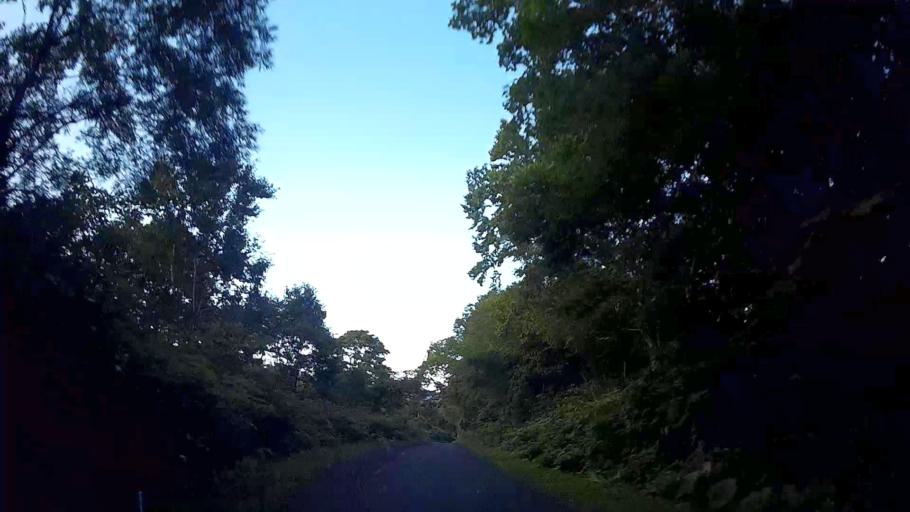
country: JP
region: Hokkaido
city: Iwanai
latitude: 42.6294
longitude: 140.0274
